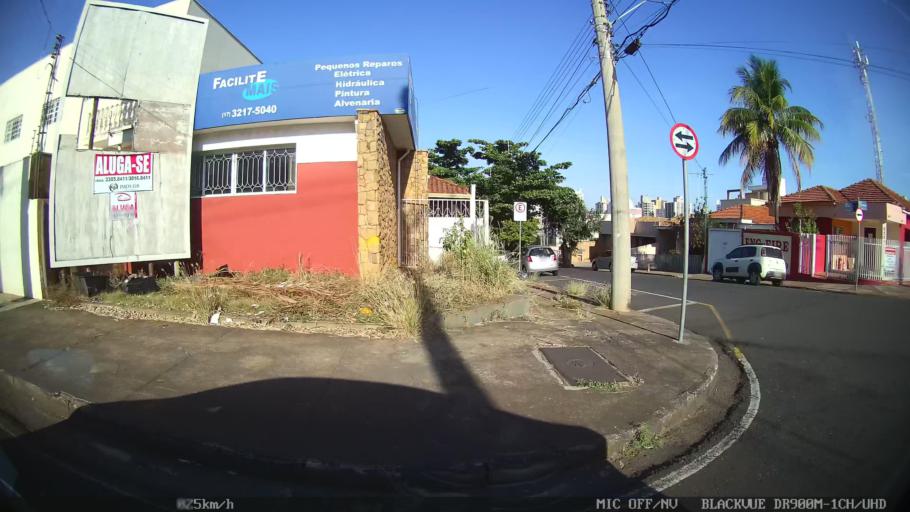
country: BR
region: Sao Paulo
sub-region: Sao Jose Do Rio Preto
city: Sao Jose do Rio Preto
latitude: -20.8114
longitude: -49.3917
